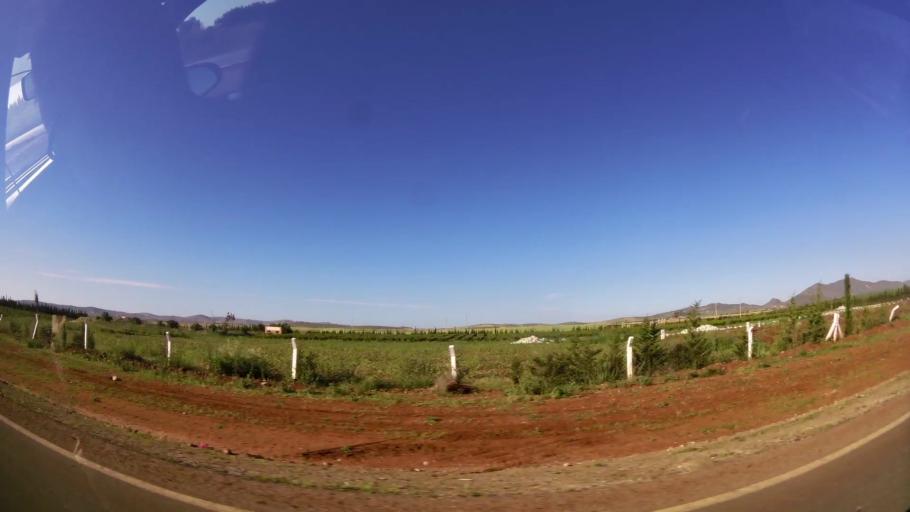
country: MA
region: Oriental
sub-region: Berkane-Taourirt
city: Ahfir
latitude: 34.9986
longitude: -2.1717
